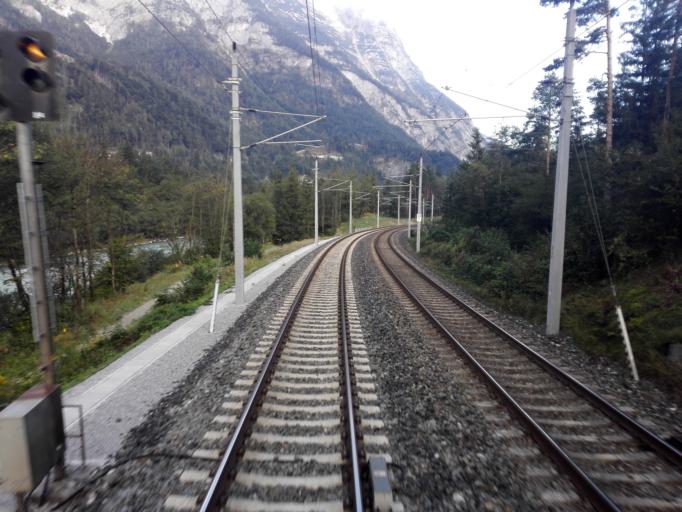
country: AT
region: Salzburg
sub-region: Politischer Bezirk Sankt Johann im Pongau
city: Werfen
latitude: 47.5148
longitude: 13.1674
